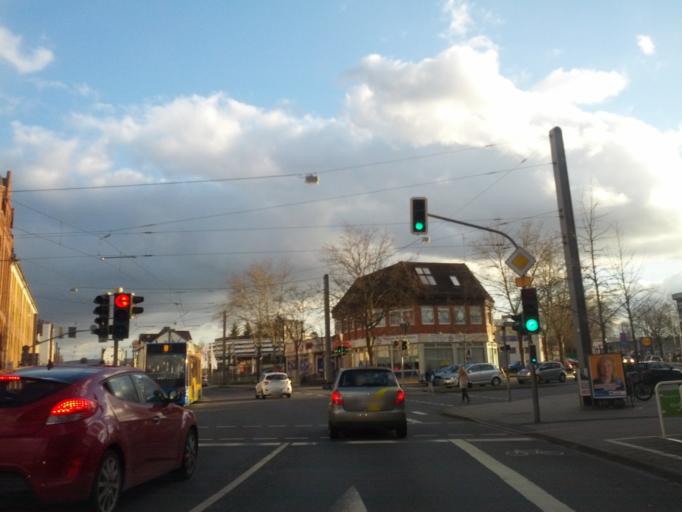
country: DE
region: Hesse
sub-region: Regierungsbezirk Kassel
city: Kassel
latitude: 51.3033
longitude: 9.5311
